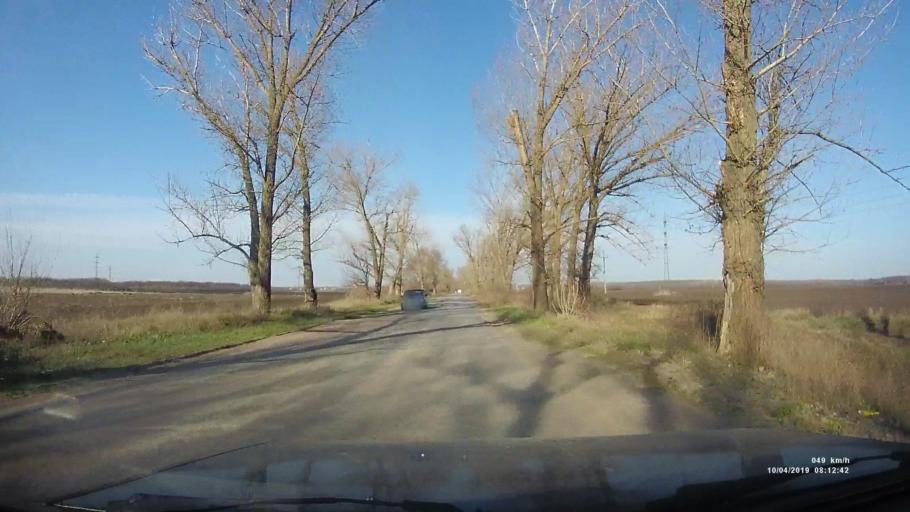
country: RU
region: Rostov
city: Masalovka
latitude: 48.3621
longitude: 40.2546
